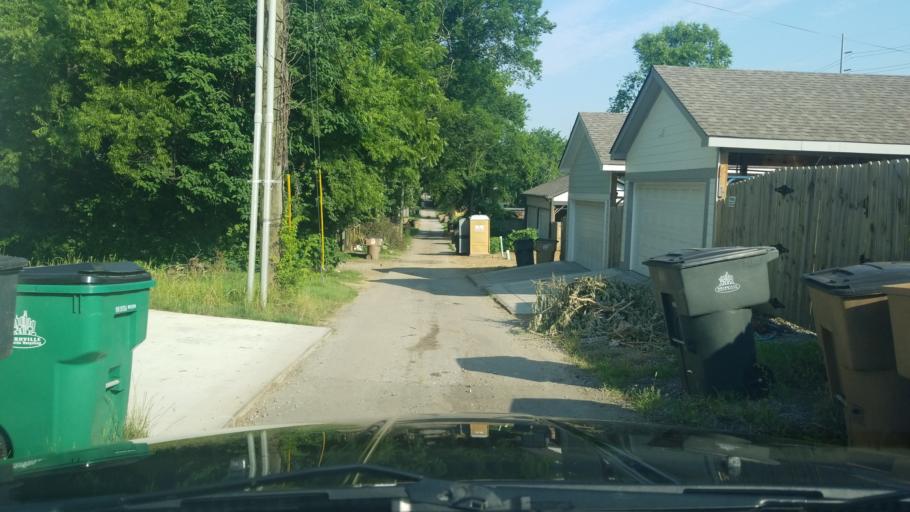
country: US
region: Tennessee
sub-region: Davidson County
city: Belle Meade
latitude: 36.1639
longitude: -86.8626
